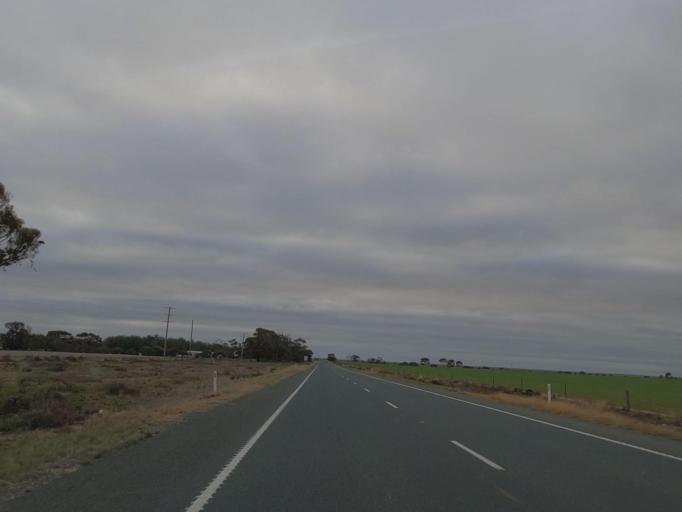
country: AU
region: Victoria
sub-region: Swan Hill
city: Swan Hill
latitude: -35.5615
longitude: 143.7818
